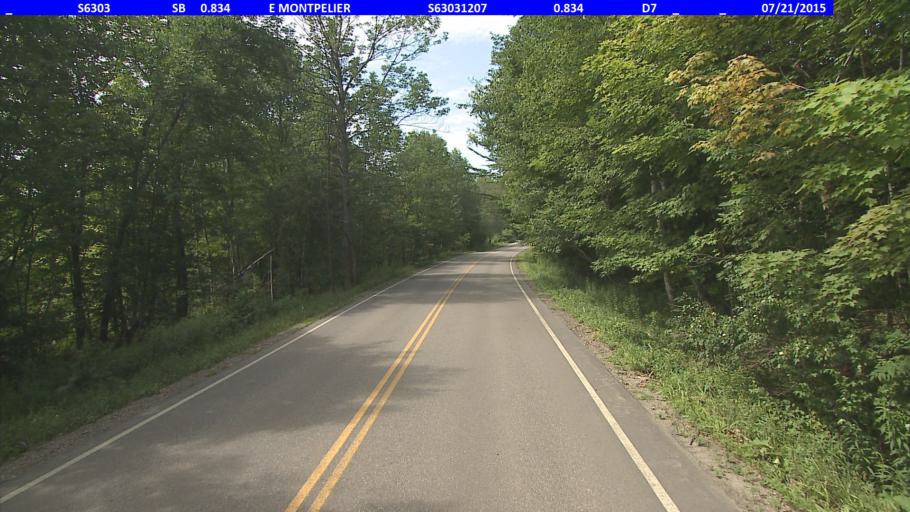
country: US
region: Vermont
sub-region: Washington County
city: Montpelier
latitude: 44.2826
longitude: -72.5479
